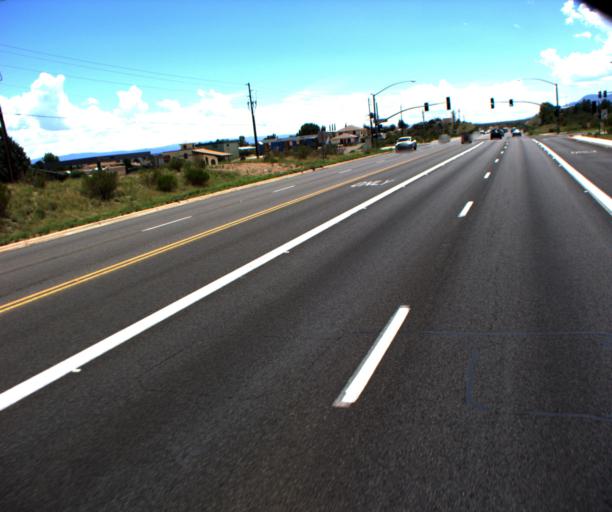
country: US
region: Arizona
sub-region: Yavapai County
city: Verde Village
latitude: 34.6932
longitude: -111.9834
